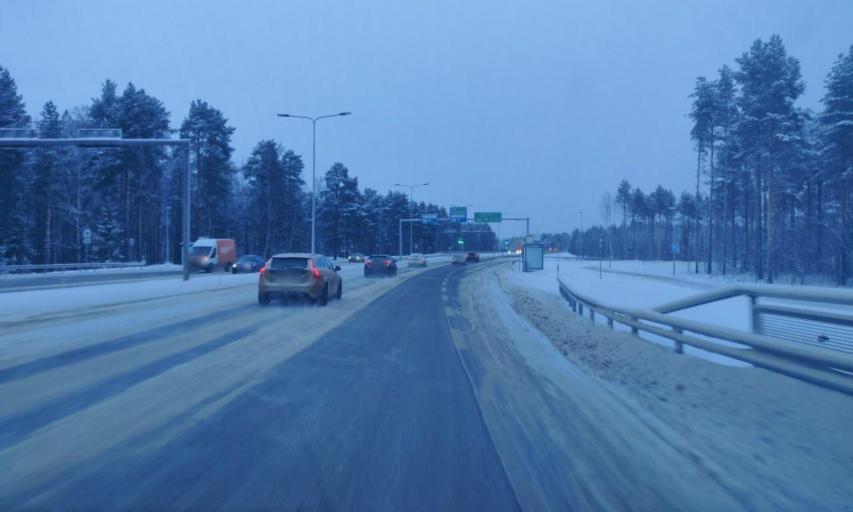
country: FI
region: Northern Ostrobothnia
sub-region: Oulu
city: Oulu
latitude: 65.0389
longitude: 25.4698
